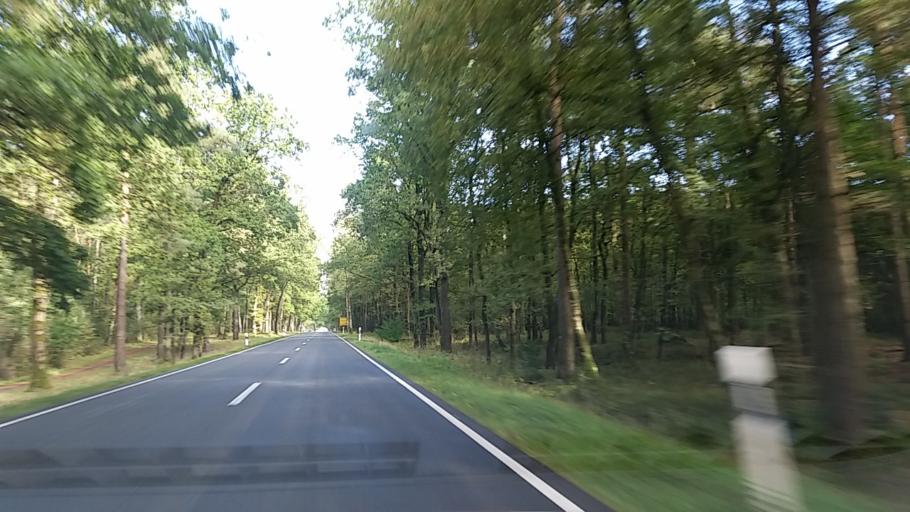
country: DE
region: Lower Saxony
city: Neuenkirchen
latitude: 53.0250
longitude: 9.6800
